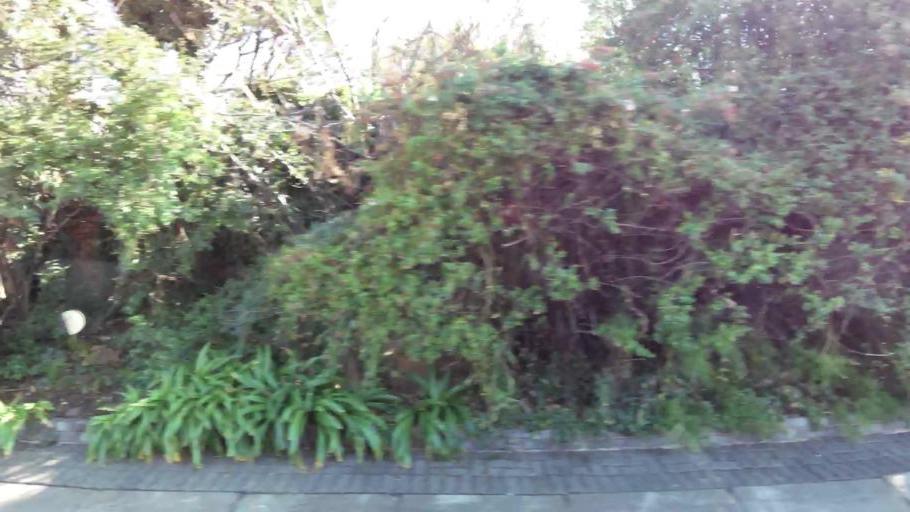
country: ZA
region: Gauteng
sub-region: City of Johannesburg Metropolitan Municipality
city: Soweto
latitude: -26.2420
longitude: 27.9090
